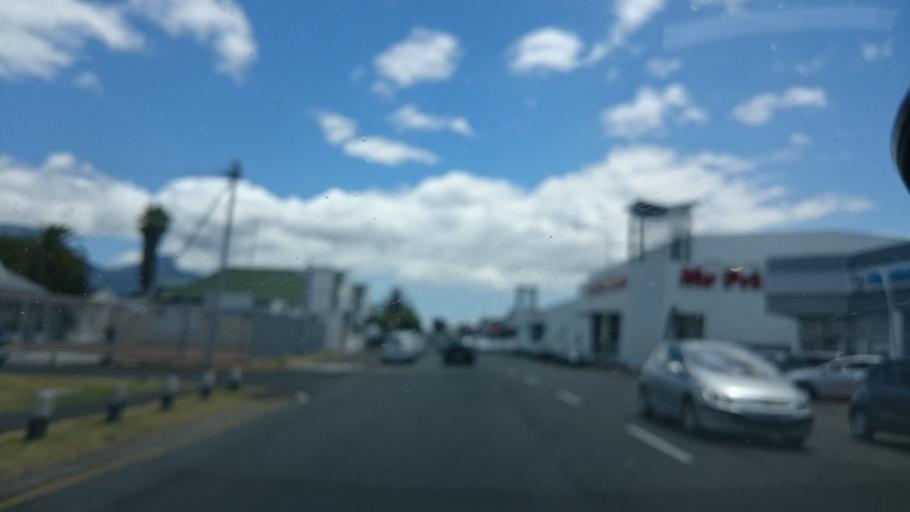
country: ZA
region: Western Cape
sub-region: City of Cape Town
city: Bergvliet
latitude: -34.0401
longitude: 18.4642
